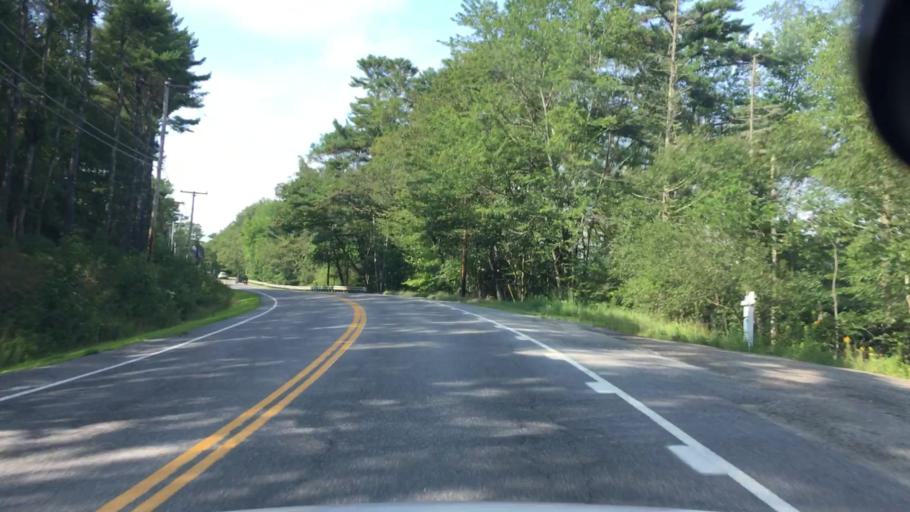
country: US
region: Maine
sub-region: Cumberland County
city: Harpswell Center
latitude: 43.8391
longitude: -69.9119
